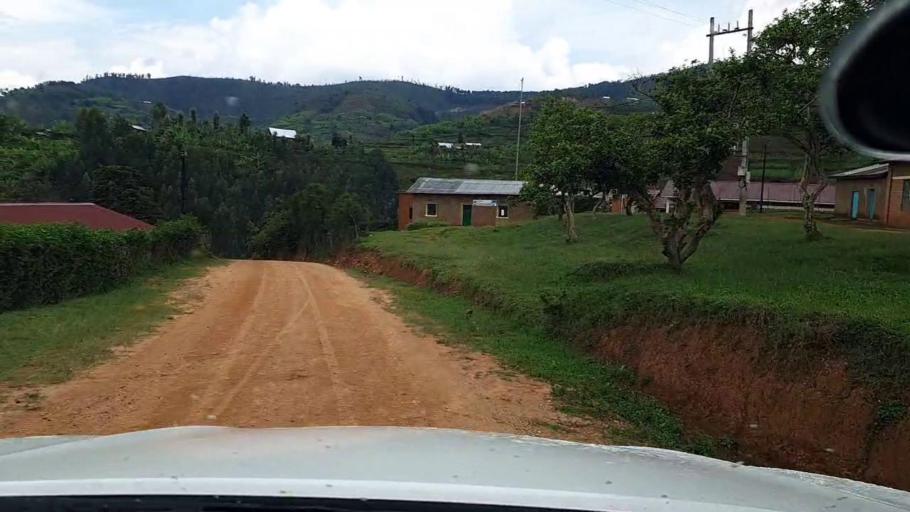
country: RW
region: Western Province
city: Kibuye
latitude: -2.1123
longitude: 29.4212
